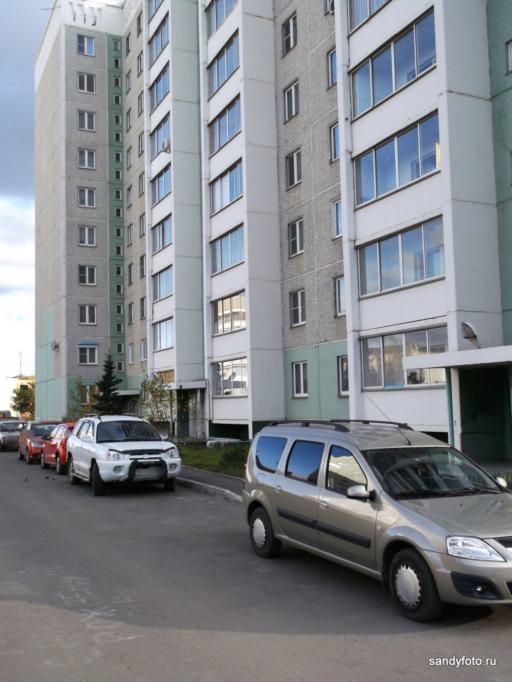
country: RU
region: Chelyabinsk
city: Troitsk
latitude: 54.0774
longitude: 61.5273
